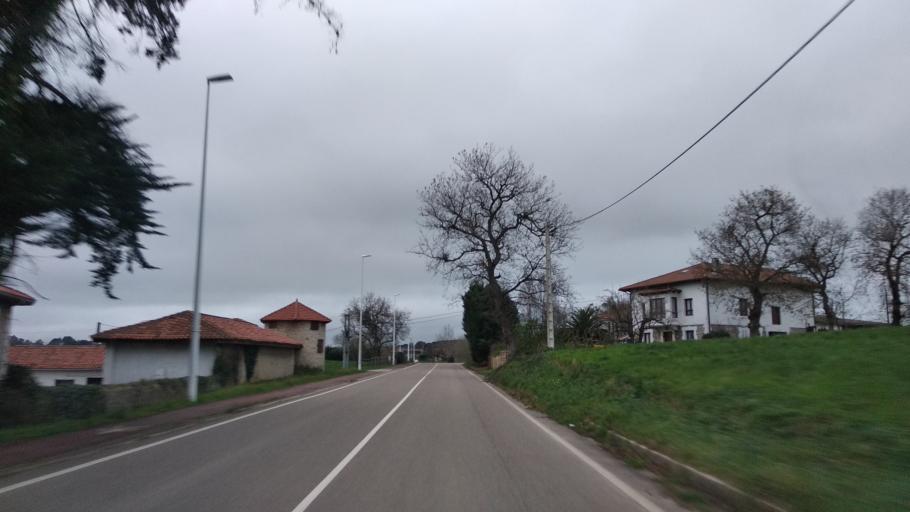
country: ES
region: Cantabria
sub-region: Provincia de Cantabria
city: Entrambasaguas
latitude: 43.4443
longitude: -3.7222
